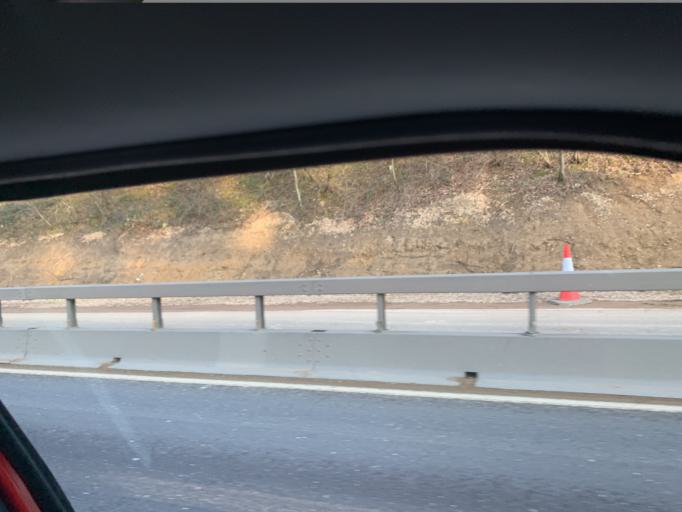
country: GB
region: England
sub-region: Surrey
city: Bletchingley
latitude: 51.2397
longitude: -0.1178
